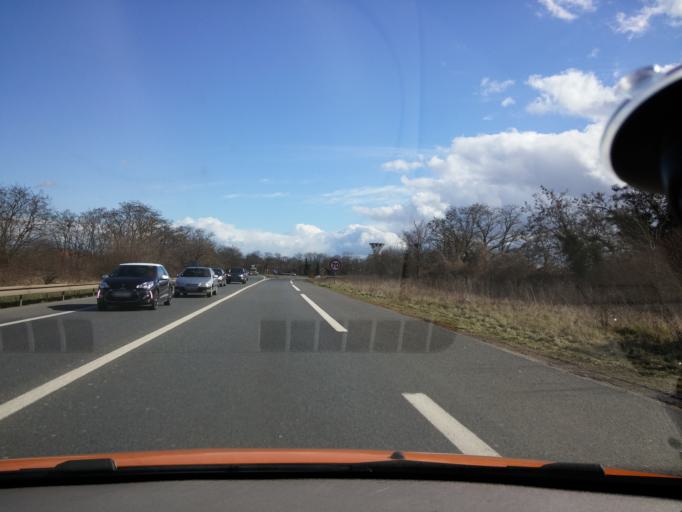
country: FR
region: Ile-de-France
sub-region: Departement de l'Essonne
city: Chilly-Mazarin
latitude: 48.7105
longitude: 2.3018
